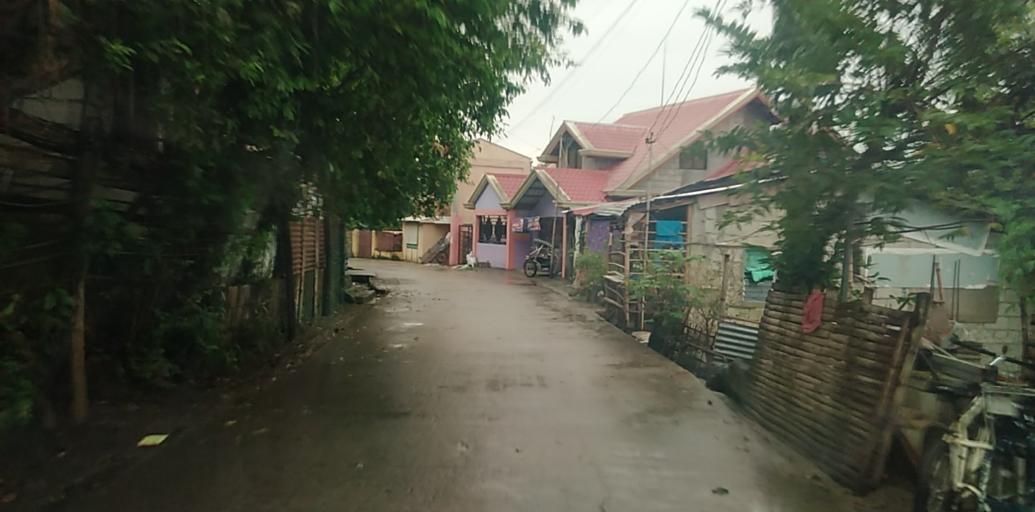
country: PH
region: Central Luzon
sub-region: Province of Pampanga
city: Arayat
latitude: 15.1581
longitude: 120.7395
